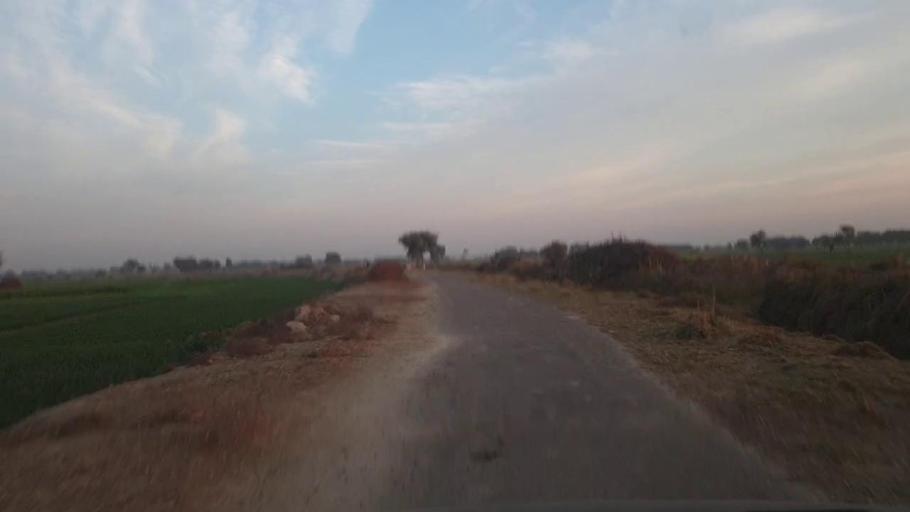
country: PK
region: Sindh
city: Shahpur Chakar
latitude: 26.0725
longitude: 68.5254
